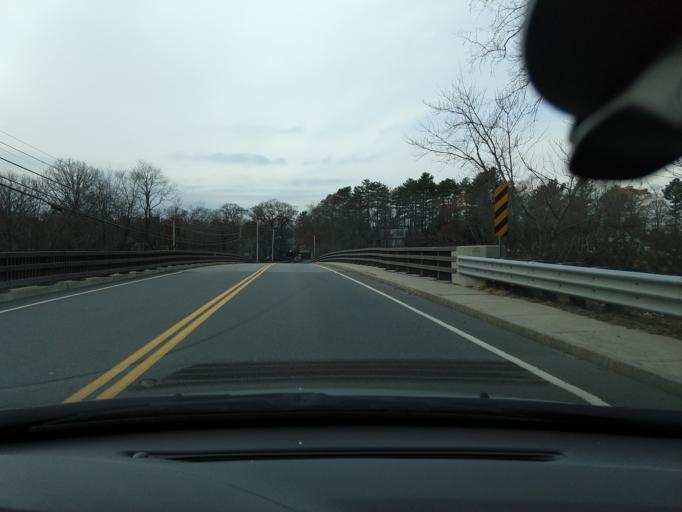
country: US
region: Massachusetts
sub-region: Middlesex County
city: Billerica
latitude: 42.5576
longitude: -71.2819
